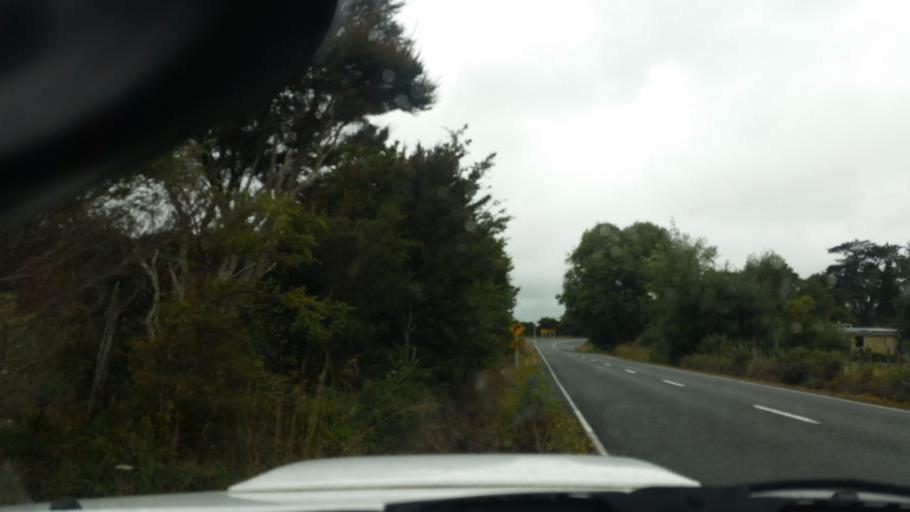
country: NZ
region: Auckland
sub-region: Auckland
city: Wellsford
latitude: -36.1397
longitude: 174.5064
